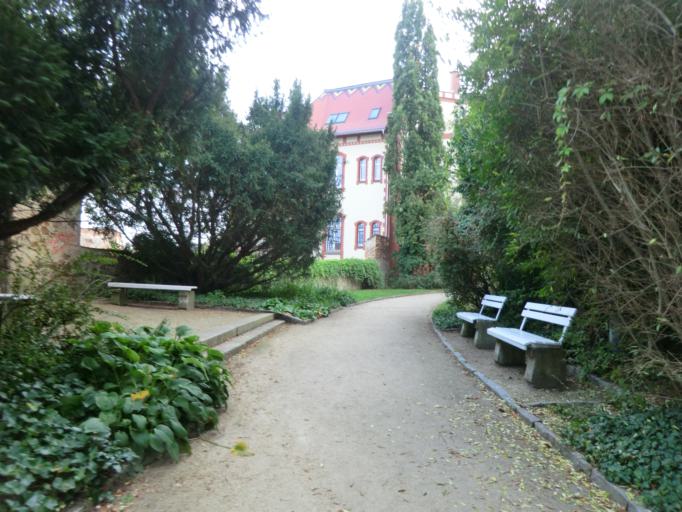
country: DE
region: Saxony
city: Goerlitz
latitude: 51.1557
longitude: 14.9946
